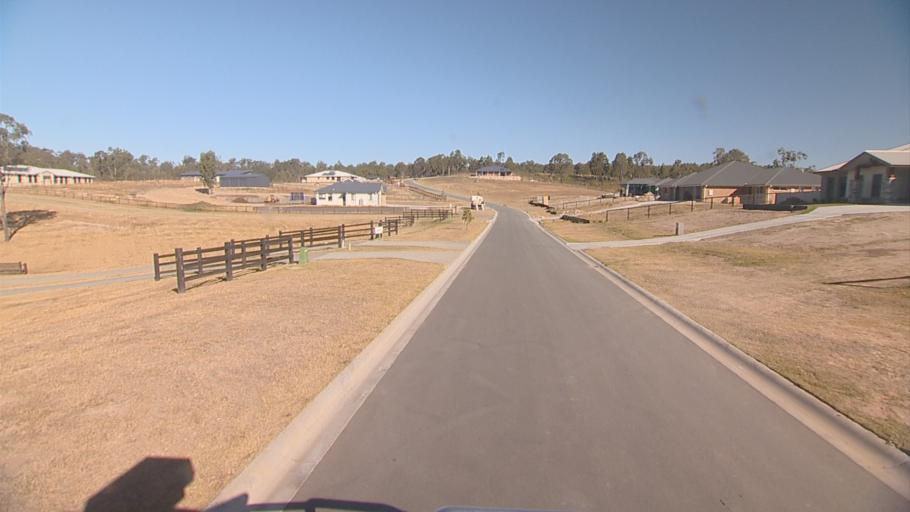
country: AU
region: Queensland
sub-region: Logan
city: Cedar Vale
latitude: -27.8748
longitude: 153.0469
